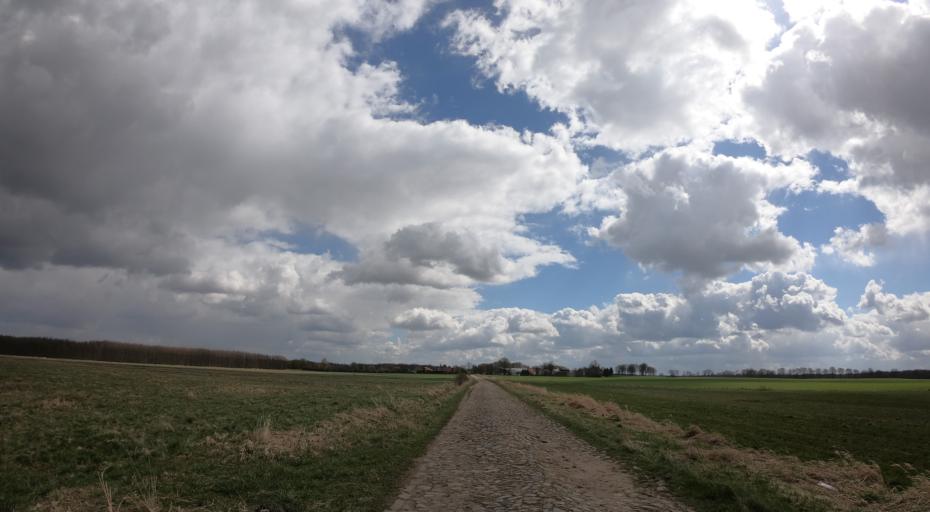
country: PL
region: West Pomeranian Voivodeship
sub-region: Powiat drawski
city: Drawsko Pomorskie
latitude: 53.5446
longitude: 15.8645
